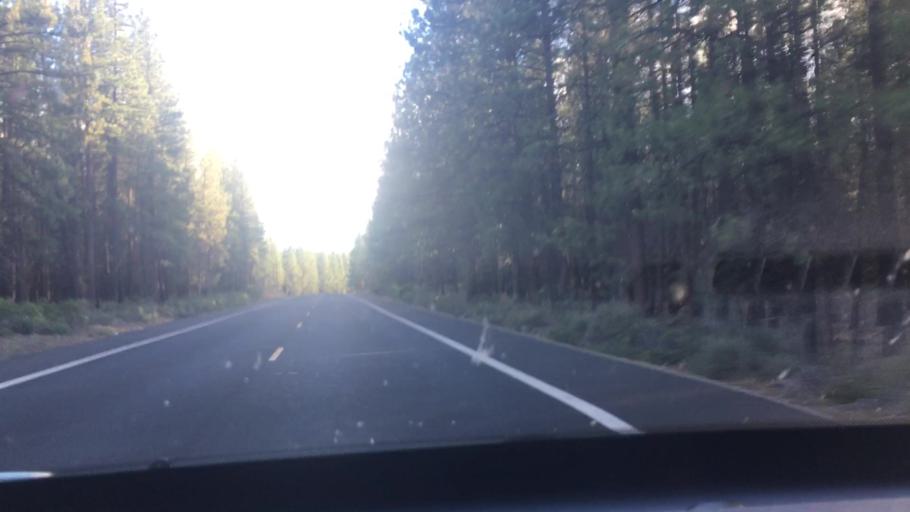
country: US
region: Oregon
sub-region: Deschutes County
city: Deschutes River Woods
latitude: 44.0405
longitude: -121.4171
